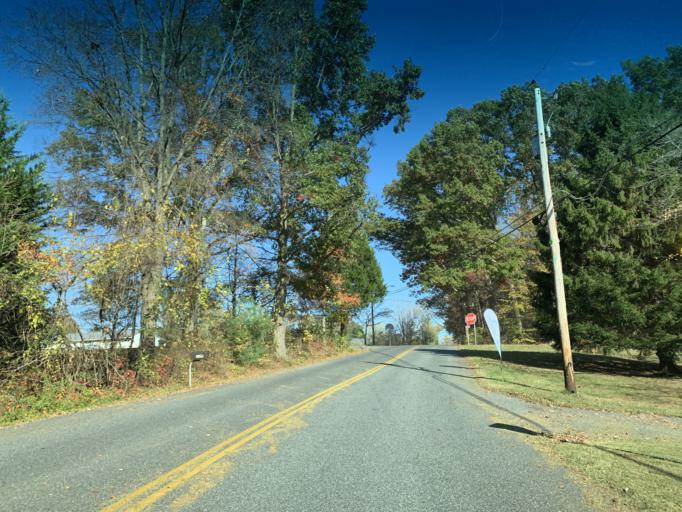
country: US
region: Maryland
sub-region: Harford County
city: Joppatowne
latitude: 39.4772
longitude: -76.3555
